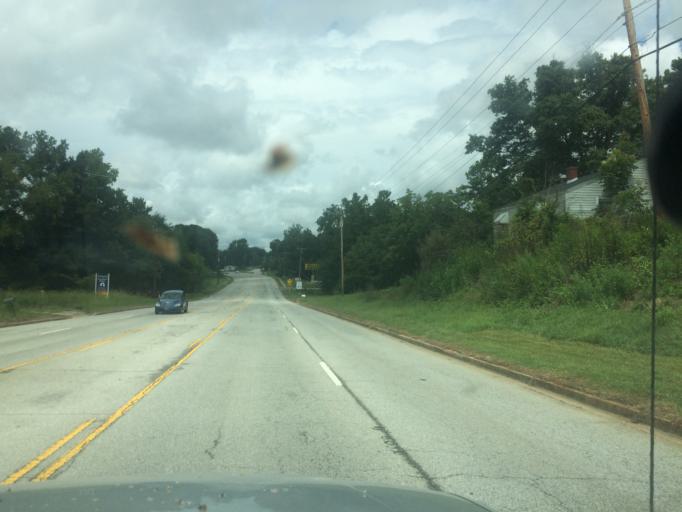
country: US
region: South Carolina
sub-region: Greenville County
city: Greer
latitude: 34.9163
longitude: -82.2118
